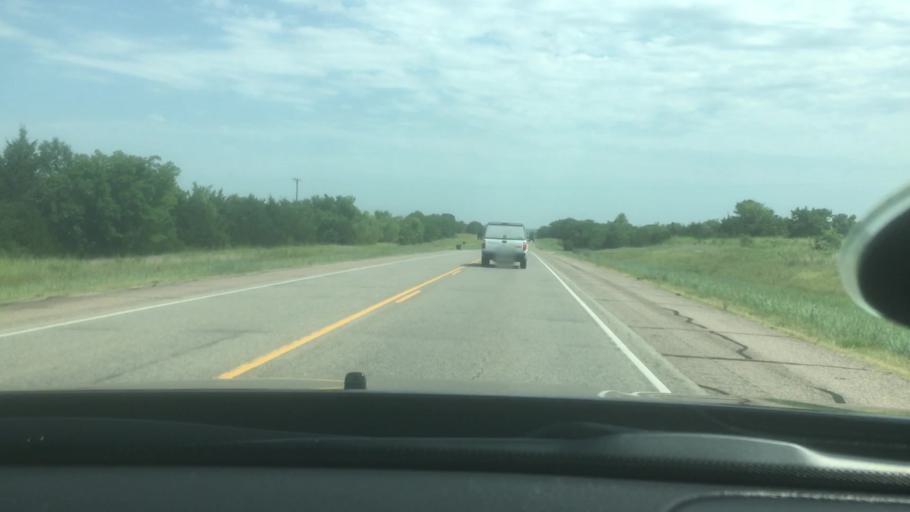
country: US
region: Oklahoma
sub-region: Seminole County
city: Maud
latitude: 35.0424
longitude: -96.9314
